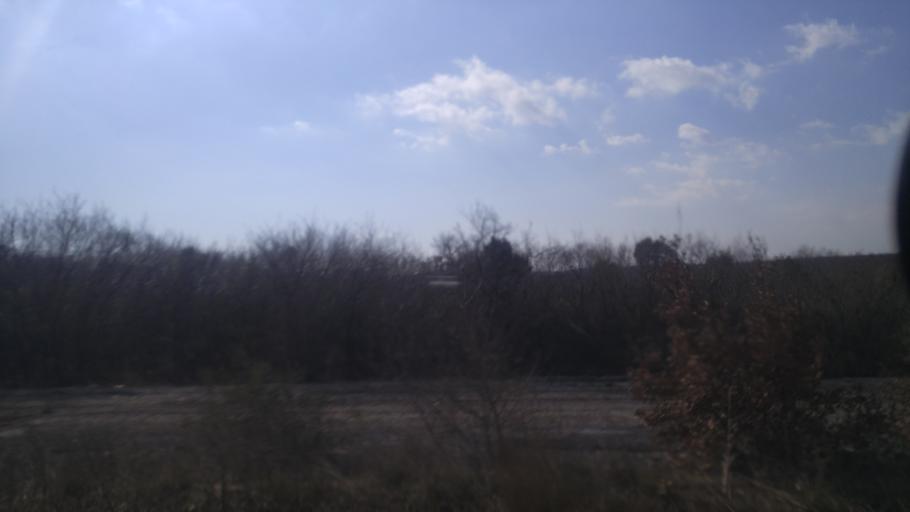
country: TR
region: Istanbul
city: Canta
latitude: 41.1669
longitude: 28.0993
